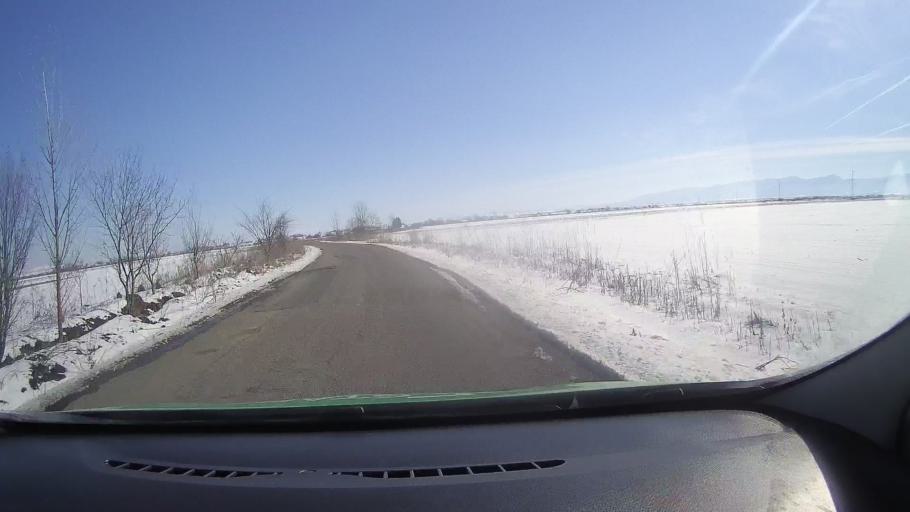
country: RO
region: Brasov
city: Fogarasch
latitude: 45.8178
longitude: 24.9907
